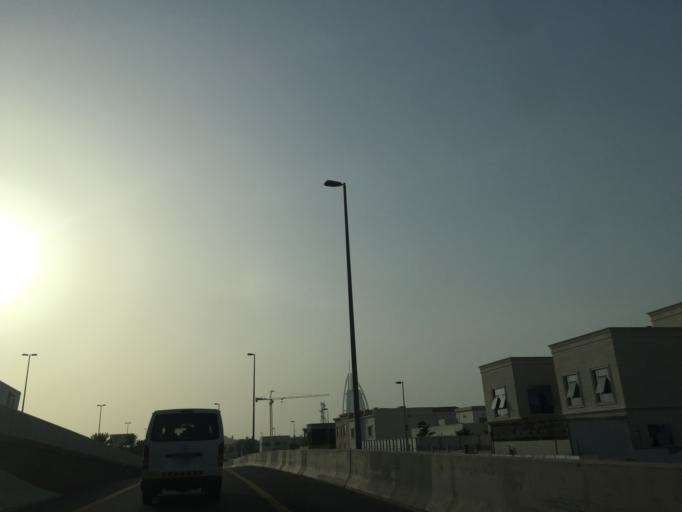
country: AE
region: Dubai
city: Dubai
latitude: 25.1245
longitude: 55.2003
